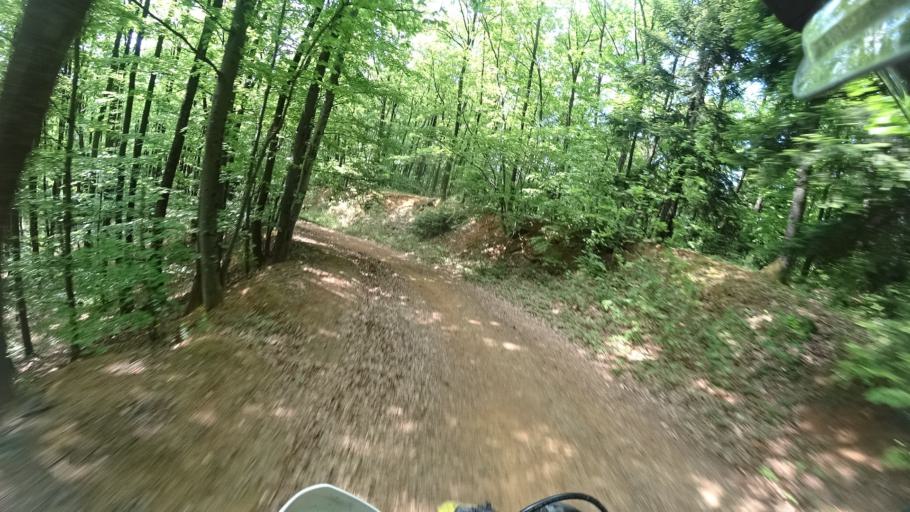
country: HR
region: Grad Zagreb
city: Kasina
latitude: 45.9353
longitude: 15.9413
